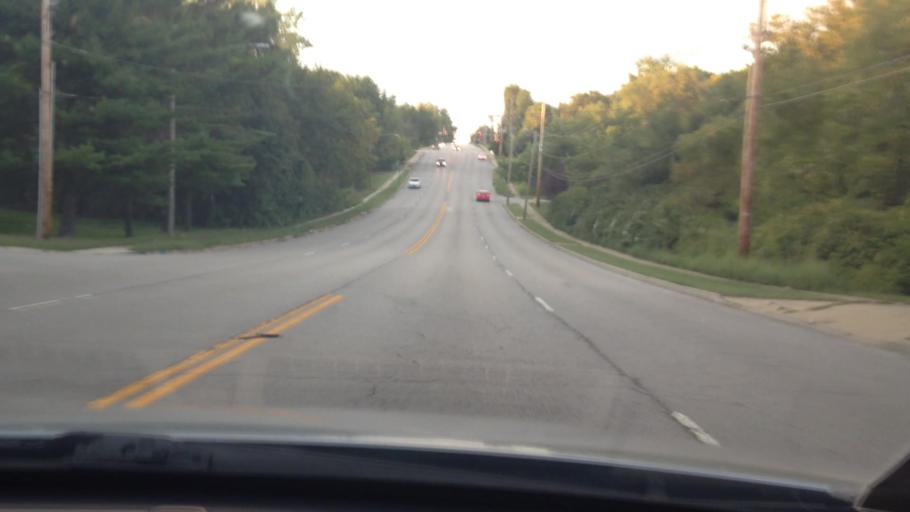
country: US
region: Missouri
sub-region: Jackson County
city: Raytown
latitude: 38.9697
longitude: -94.4652
